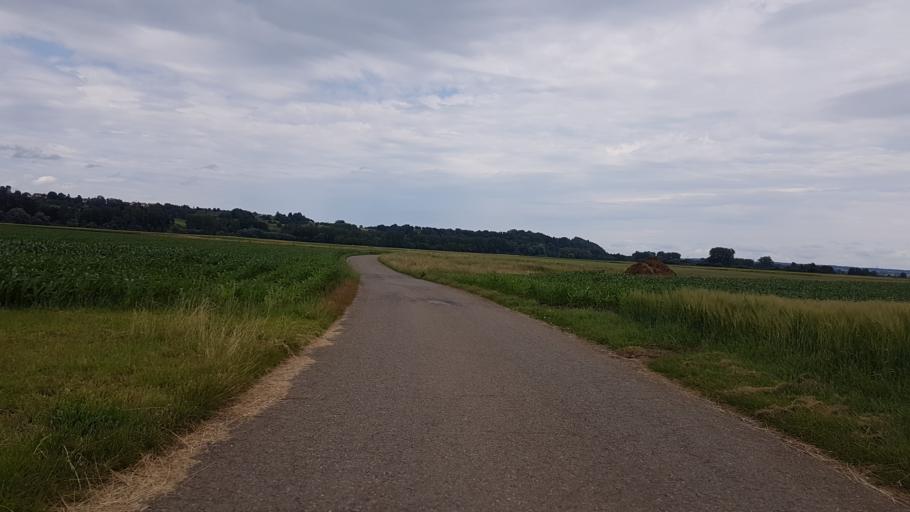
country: DE
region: Baden-Wuerttemberg
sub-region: Tuebingen Region
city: Mengen
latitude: 48.0626
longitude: 9.3612
